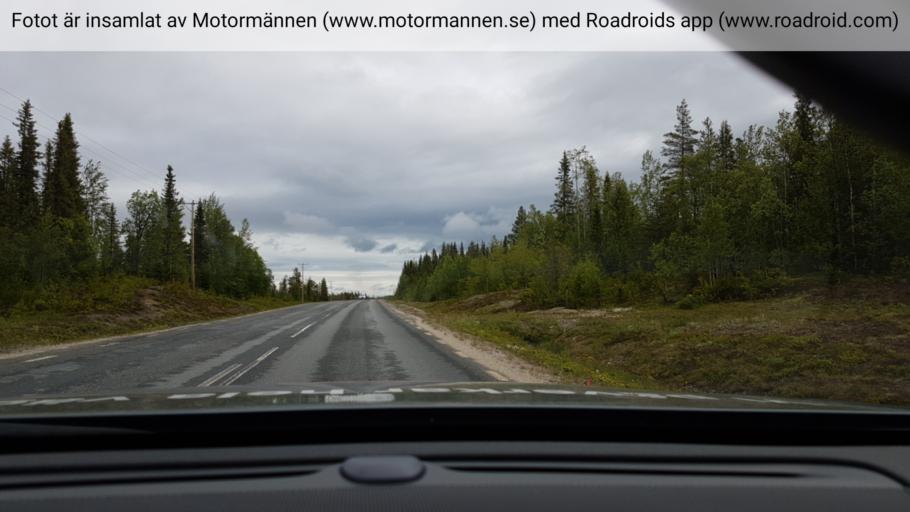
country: SE
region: Vaesterbotten
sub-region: Lycksele Kommun
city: Soderfors
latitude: 64.4096
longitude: 18.0163
